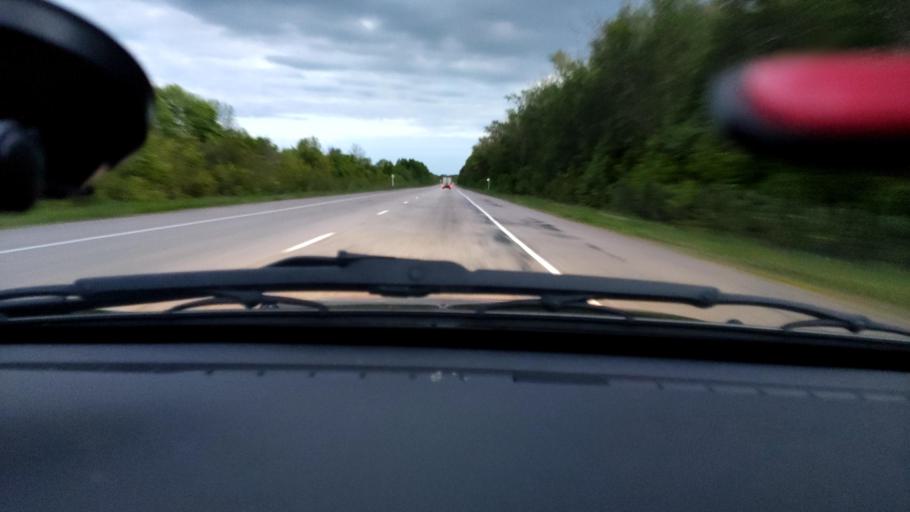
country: RU
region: Voronezj
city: Kolodeznyy
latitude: 51.2768
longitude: 39.0456
